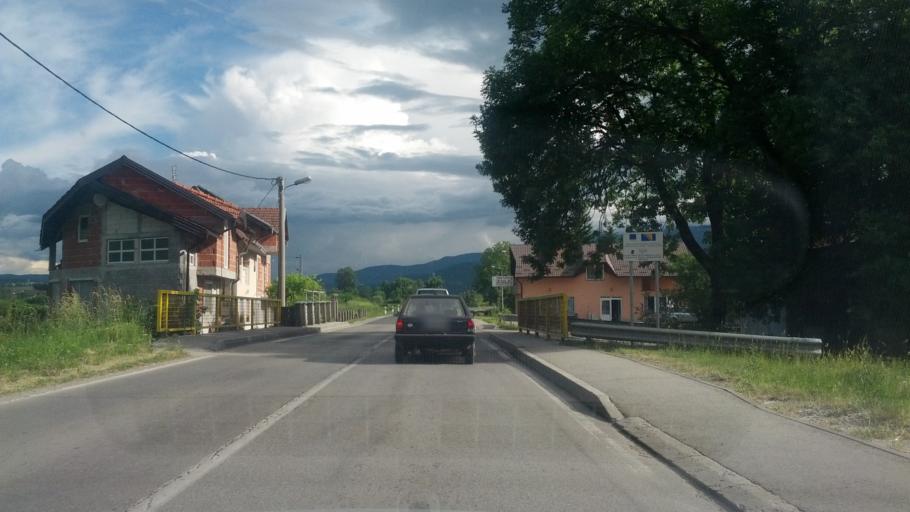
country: BA
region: Federation of Bosnia and Herzegovina
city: Bihac
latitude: 44.8538
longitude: 15.8822
